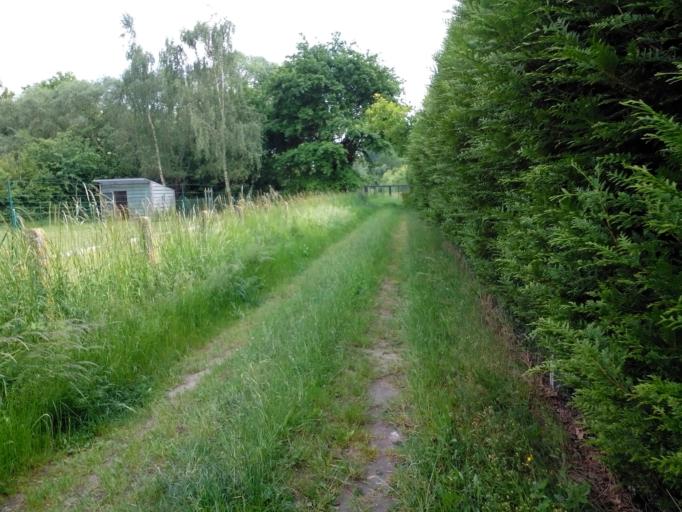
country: BE
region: Flanders
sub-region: Provincie Vlaams-Brabant
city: Rotselaar
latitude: 50.9729
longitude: 4.7224
